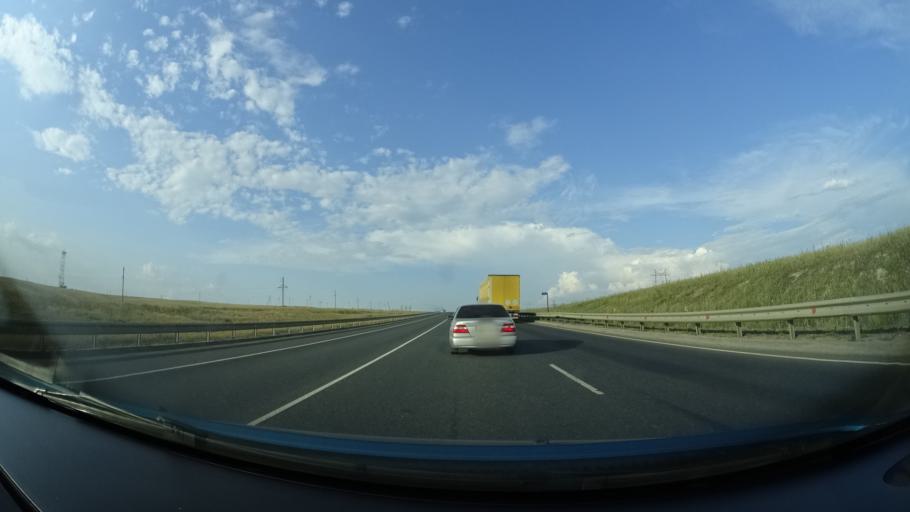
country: RU
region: Samara
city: Krasnyy Yar
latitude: 53.6929
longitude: 50.7960
